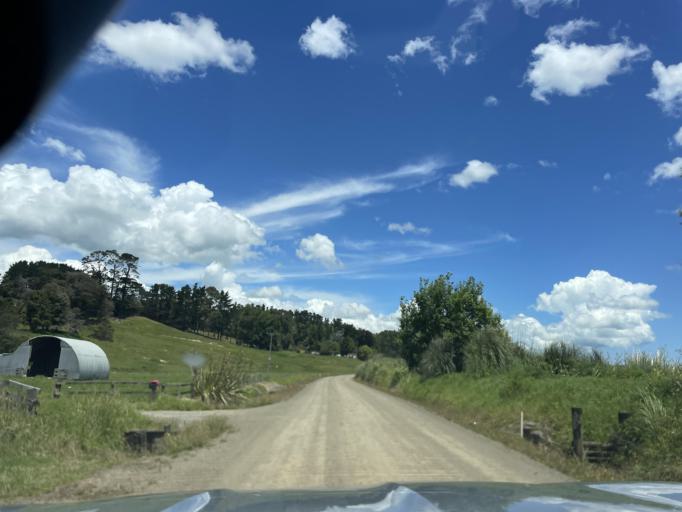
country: NZ
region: Northland
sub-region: Kaipara District
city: Dargaville
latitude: -35.9038
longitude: 173.9220
